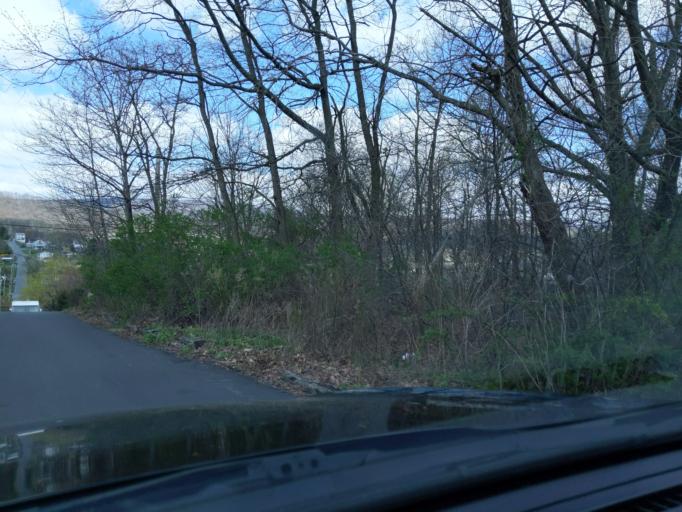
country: US
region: Pennsylvania
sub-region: Blair County
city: Altoona
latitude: 40.5301
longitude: -78.4010
